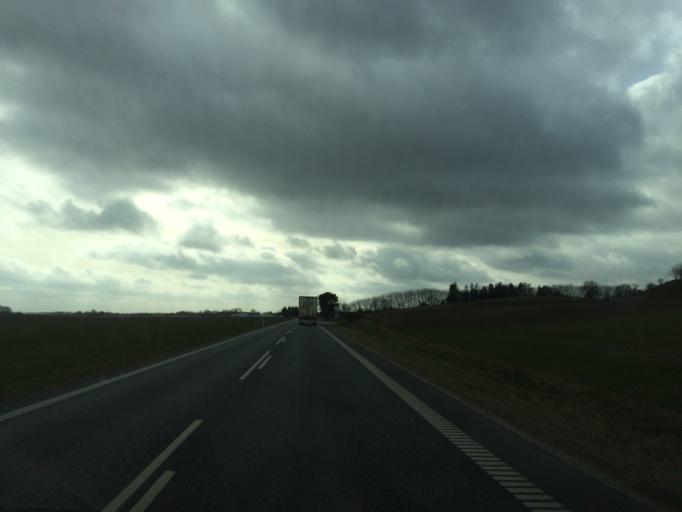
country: DK
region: Central Jutland
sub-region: Favrskov Kommune
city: Ulstrup
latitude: 56.4977
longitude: 9.7267
